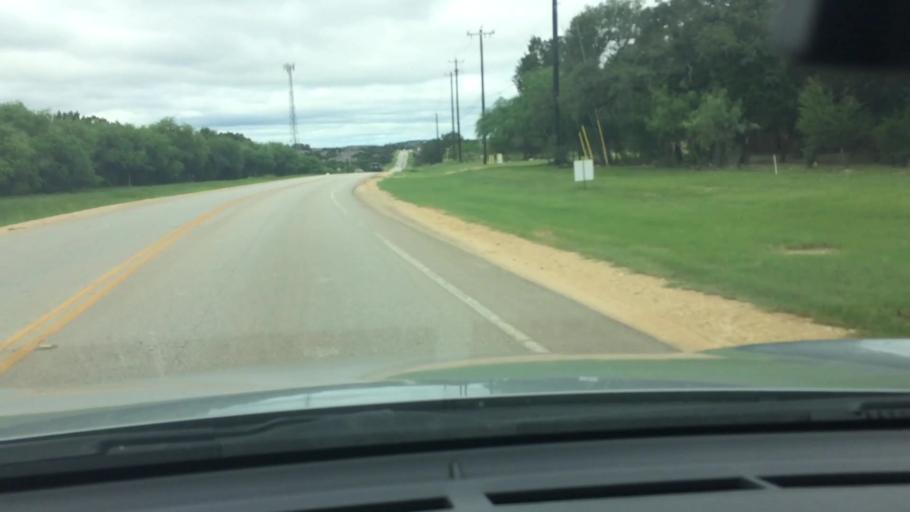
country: US
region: Texas
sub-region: Comal County
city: Garden Ridge
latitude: 29.6427
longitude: -98.3891
